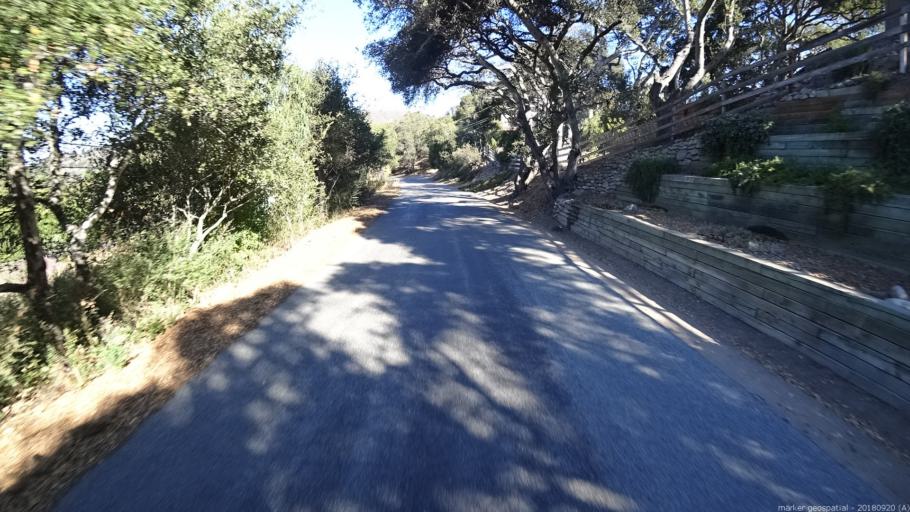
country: US
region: California
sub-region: Monterey County
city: Carmel Valley Village
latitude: 36.5196
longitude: -121.7893
